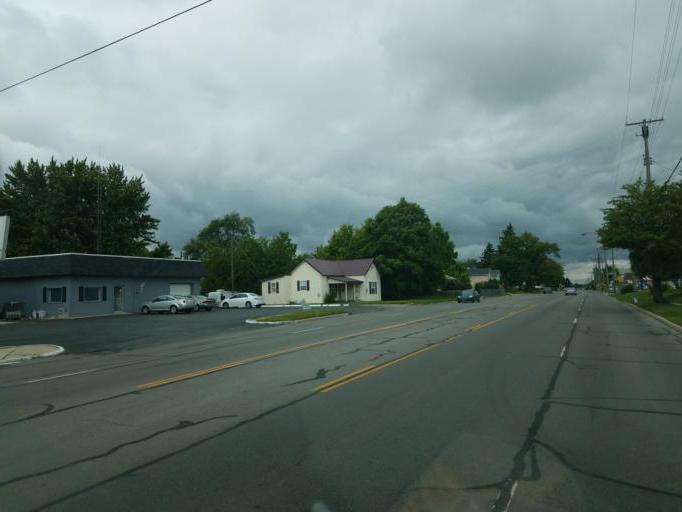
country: US
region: Ohio
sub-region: Marion County
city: Marion
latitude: 40.6043
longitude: -83.1298
